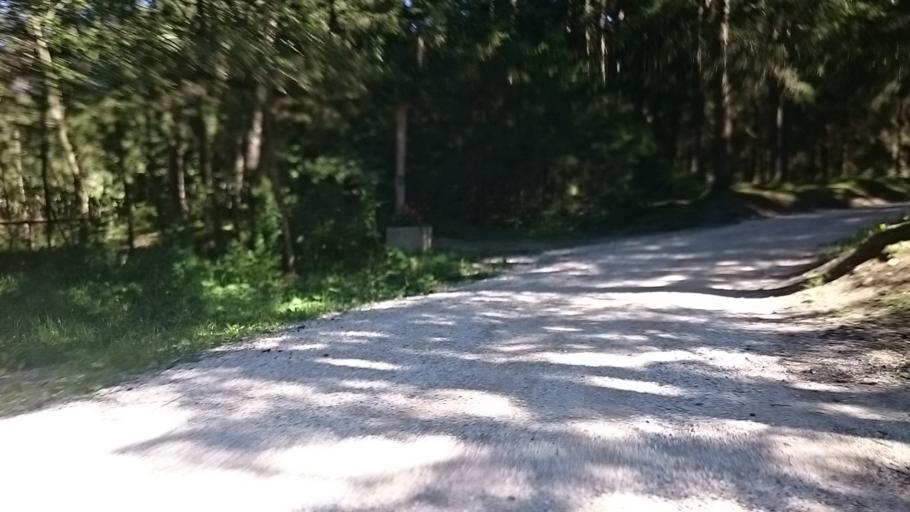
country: IT
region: Trentino-Alto Adige
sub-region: Bolzano
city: Perca
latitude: 46.7890
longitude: 11.9881
